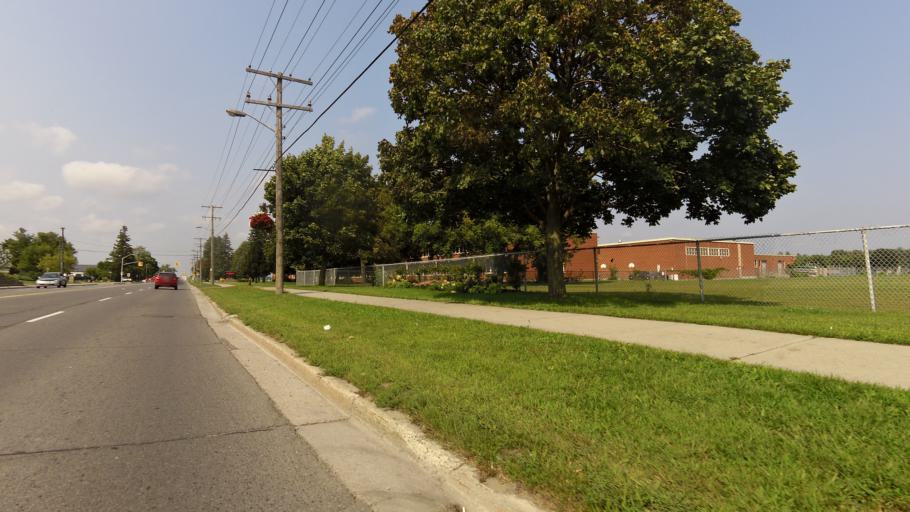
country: CA
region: Ontario
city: Prescott
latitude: 44.7185
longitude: -75.5214
